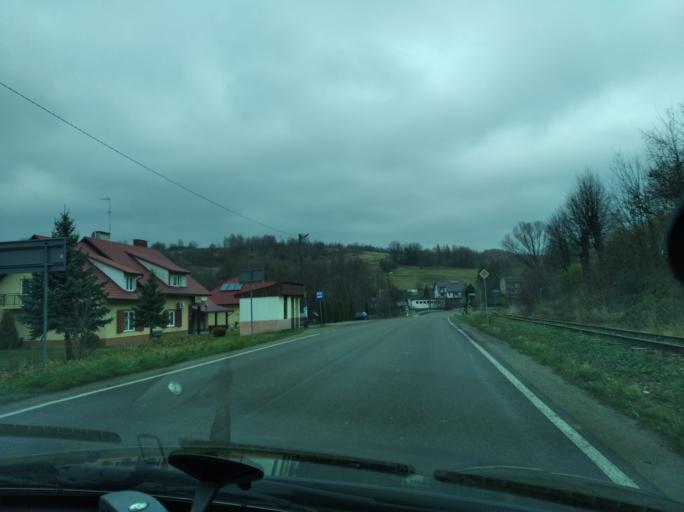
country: PL
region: Subcarpathian Voivodeship
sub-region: Powiat przeworski
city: Jawornik Polski
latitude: 49.9115
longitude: 22.2988
